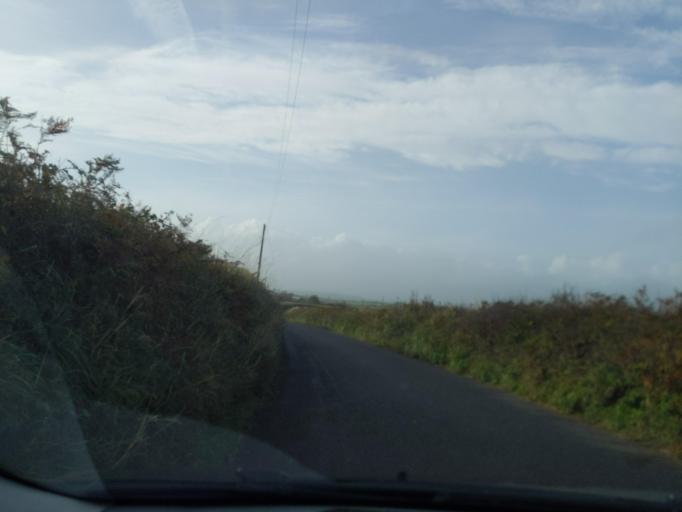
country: GB
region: England
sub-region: Cornwall
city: Pillaton
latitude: 50.3638
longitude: -4.3443
